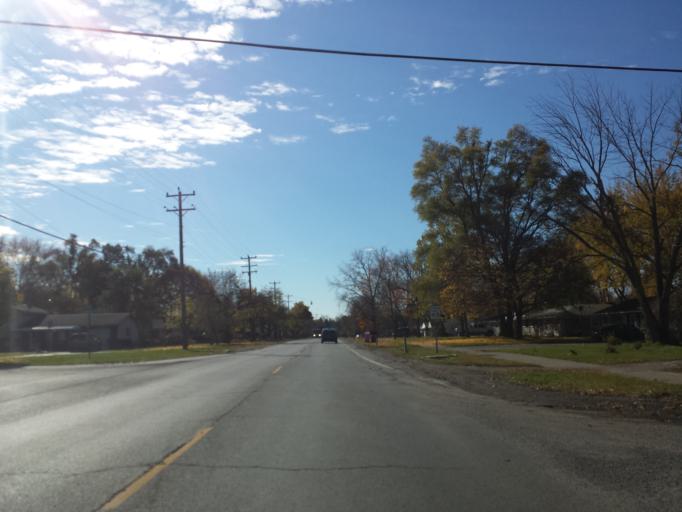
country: US
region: Michigan
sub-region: Oakland County
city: Waterford
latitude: 42.6858
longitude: -83.4172
